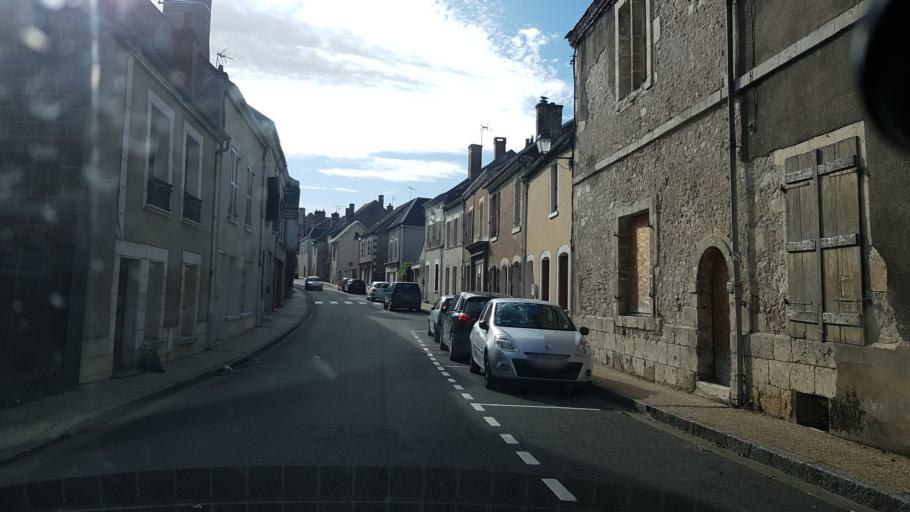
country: FR
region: Centre
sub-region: Departement du Loiret
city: Bonny-sur-Loire
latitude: 47.5616
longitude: 2.8380
